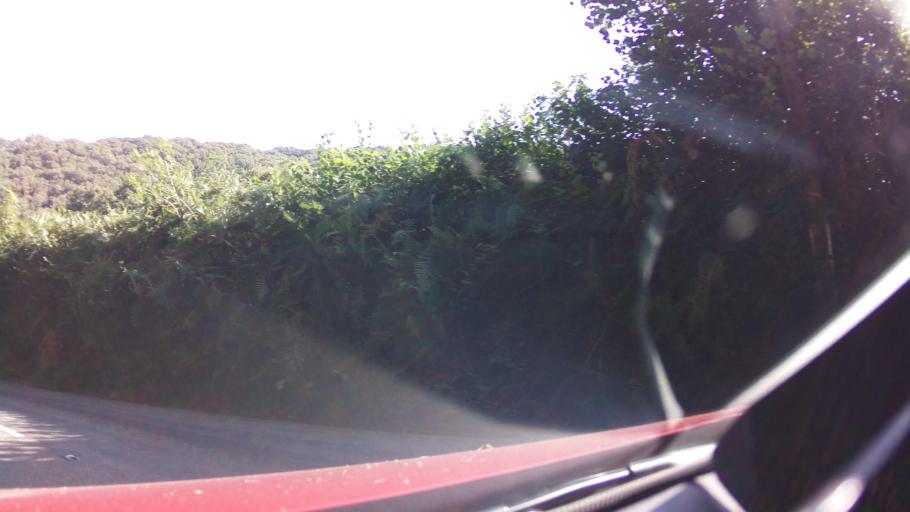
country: GB
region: England
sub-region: Devon
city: Buckfastleigh
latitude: 50.5215
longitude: -3.8057
